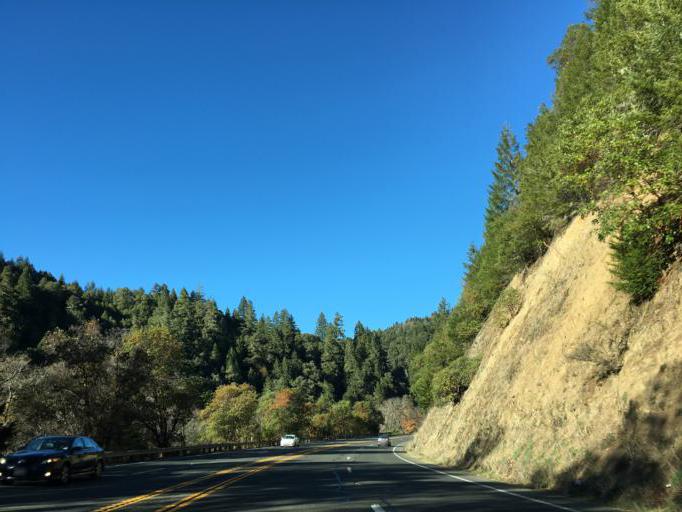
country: US
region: California
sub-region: Mendocino County
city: Brooktrails
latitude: 39.5305
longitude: -123.4043
